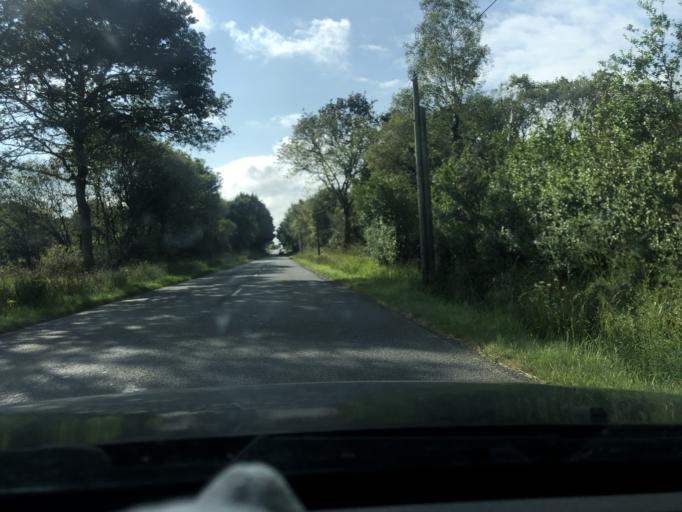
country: FR
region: Brittany
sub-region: Departement du Morbihan
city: Sainte-Helene
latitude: 47.6921
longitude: -3.2366
